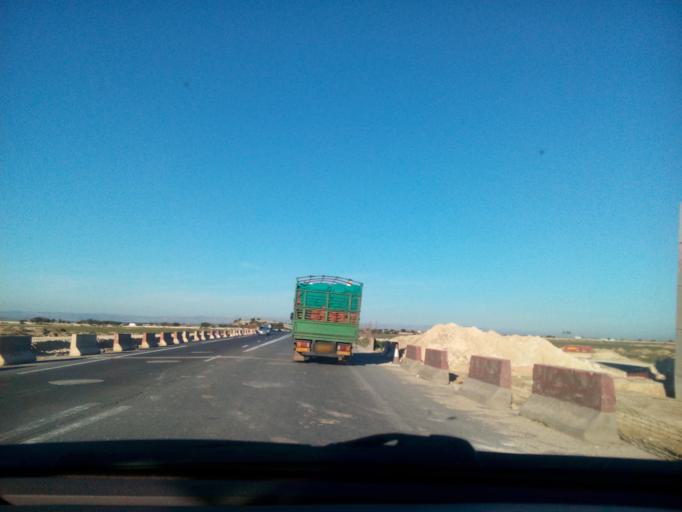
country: DZ
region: Relizane
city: Relizane
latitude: 35.7920
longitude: 0.5350
